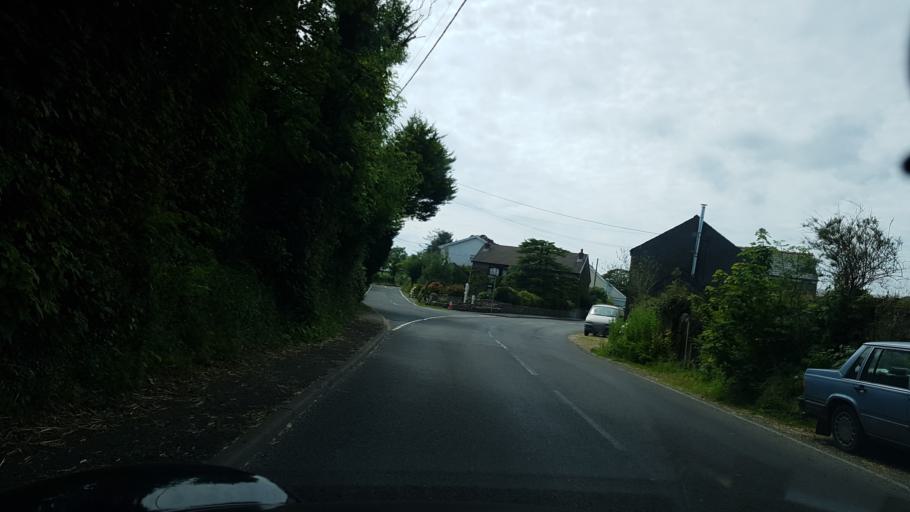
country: GB
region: Wales
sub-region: Carmarthenshire
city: Whitland
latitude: 51.7830
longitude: -4.6368
